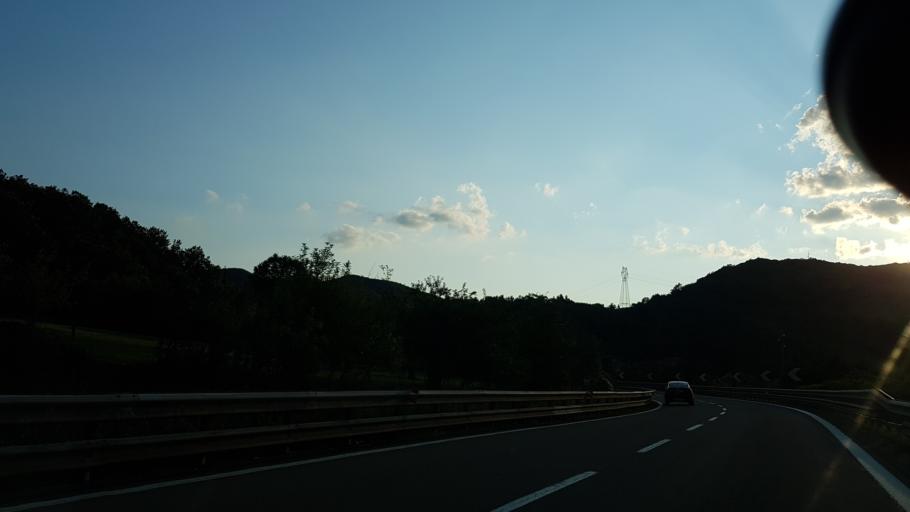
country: IT
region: Liguria
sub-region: Provincia di Genova
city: Borgo Fornari-Pieve
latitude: 44.5941
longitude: 8.9436
